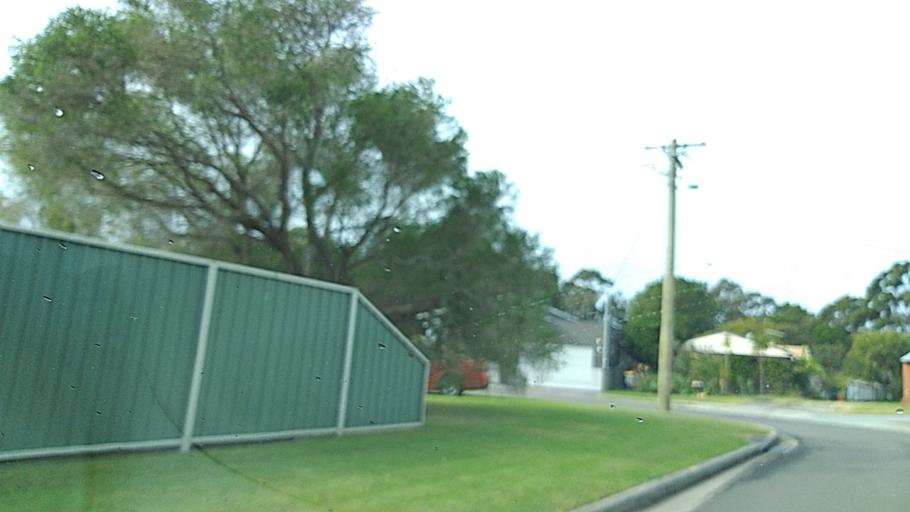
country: AU
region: New South Wales
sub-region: Wollongong
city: Bulli
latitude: -34.3368
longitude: 150.9173
